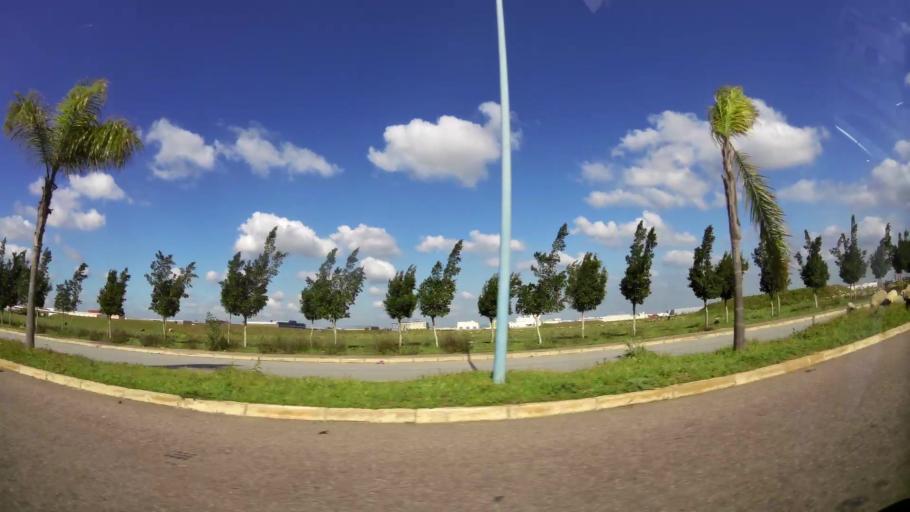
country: MA
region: Grand Casablanca
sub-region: Mediouna
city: Mediouna
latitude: 33.3985
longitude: -7.5547
